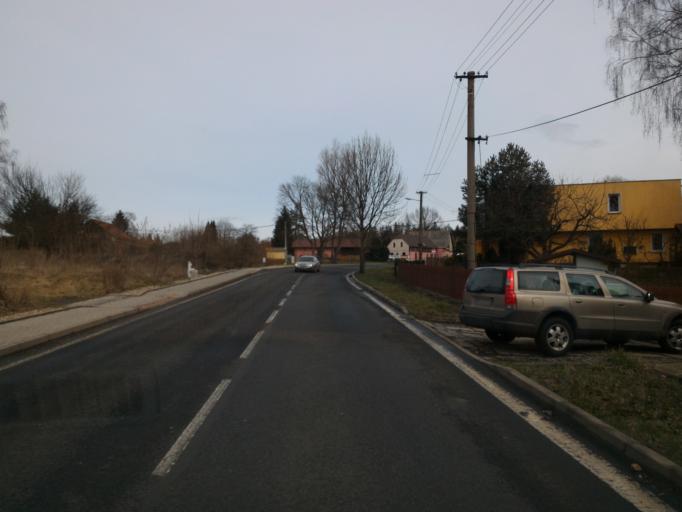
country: CZ
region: Ustecky
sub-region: Okres Decin
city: Rumburk
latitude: 50.9655
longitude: 14.5604
